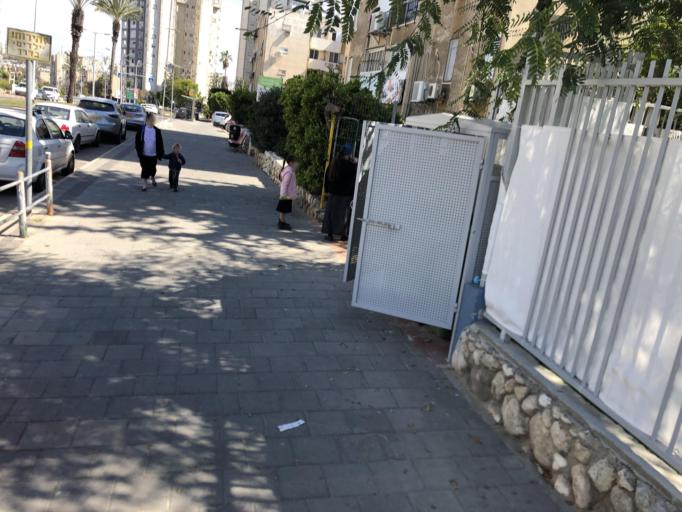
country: IL
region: Tel Aviv
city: Bat Yam
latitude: 32.0102
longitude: 34.7538
